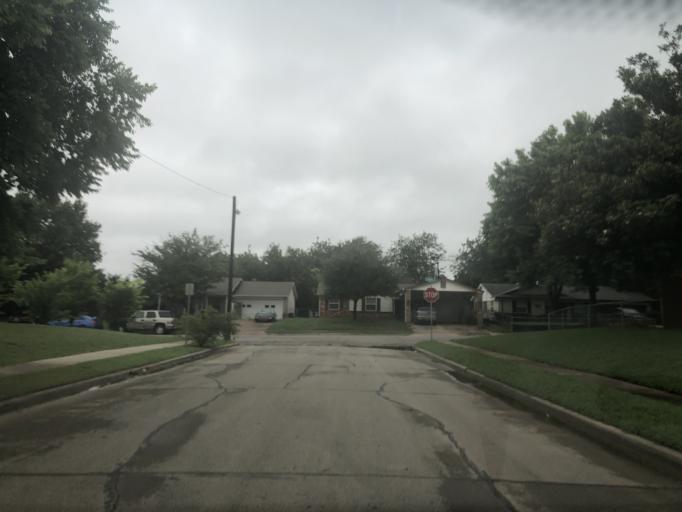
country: US
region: Texas
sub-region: Dallas County
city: Irving
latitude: 32.7952
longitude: -96.9483
